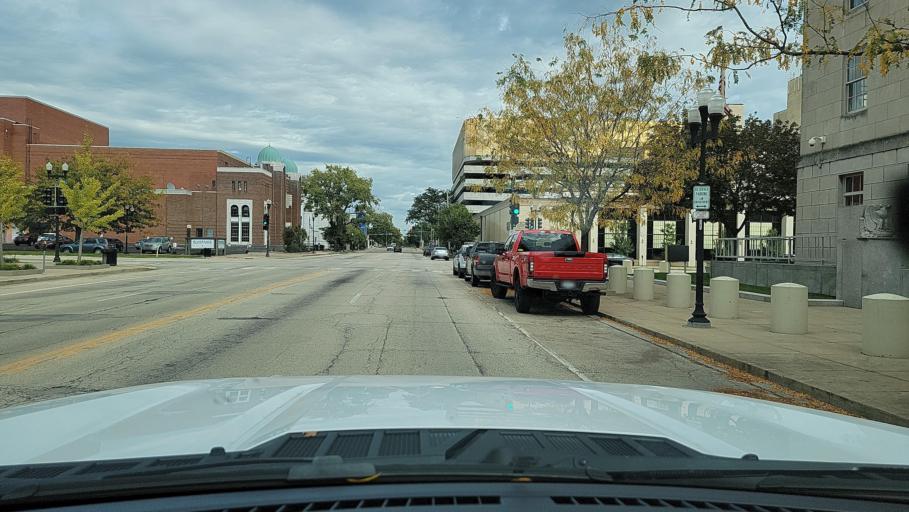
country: US
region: Illinois
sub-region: Peoria County
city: Peoria
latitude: 40.6952
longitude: -89.5919
